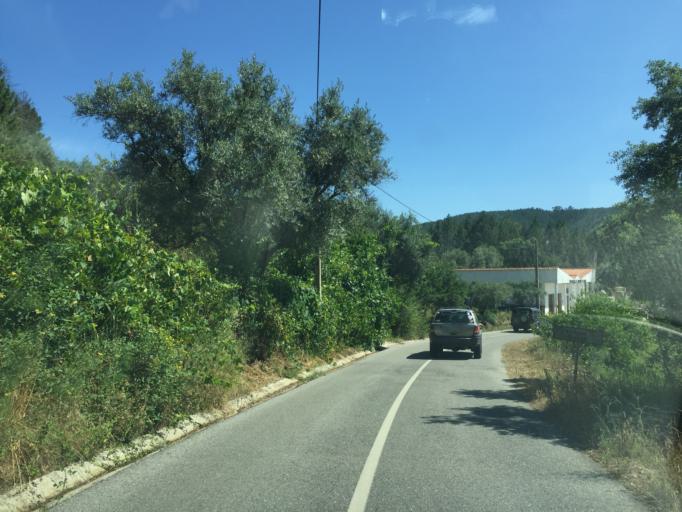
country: PT
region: Coimbra
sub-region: Pampilhosa da Serra
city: Pampilhosa da Serra
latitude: 40.0444
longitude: -7.8106
